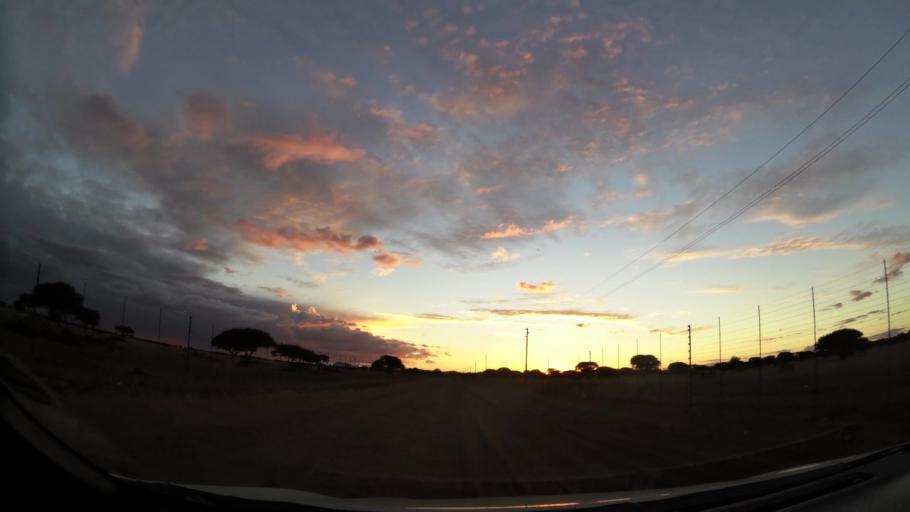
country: ZA
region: Limpopo
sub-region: Capricorn District Municipality
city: Polokwane
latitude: -23.7373
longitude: 29.4396
